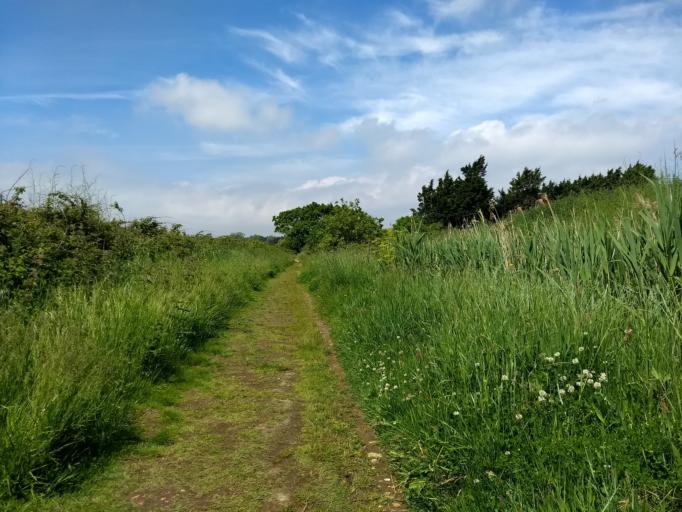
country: GB
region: England
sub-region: Isle of Wight
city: Bembridge
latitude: 50.6916
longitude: -1.1053
